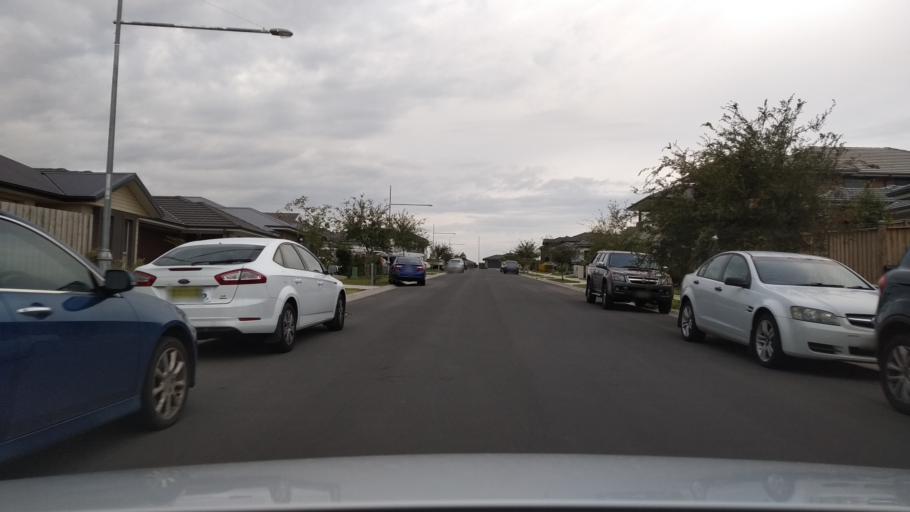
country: AU
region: New South Wales
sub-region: Camden
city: Narellan
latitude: -34.0000
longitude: 150.7288
